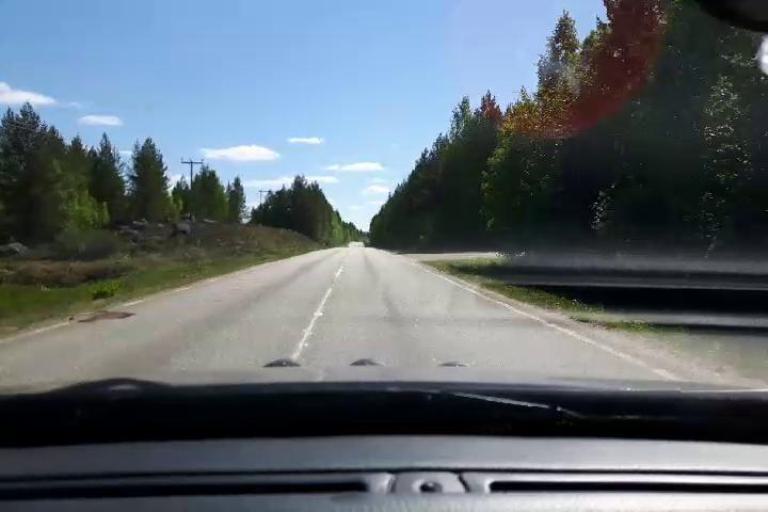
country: SE
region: Vaesternorrland
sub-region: Ange Kommun
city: Ange
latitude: 62.0830
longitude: 15.0963
